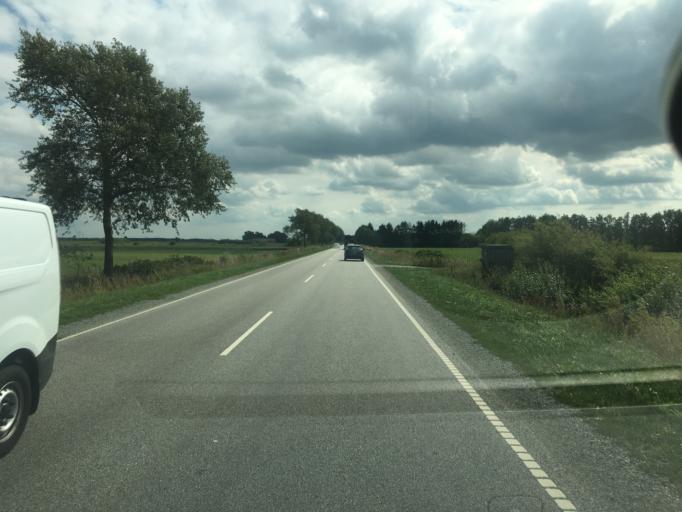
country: DK
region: South Denmark
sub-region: Aabenraa Kommune
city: Tinglev
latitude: 54.9772
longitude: 9.2998
